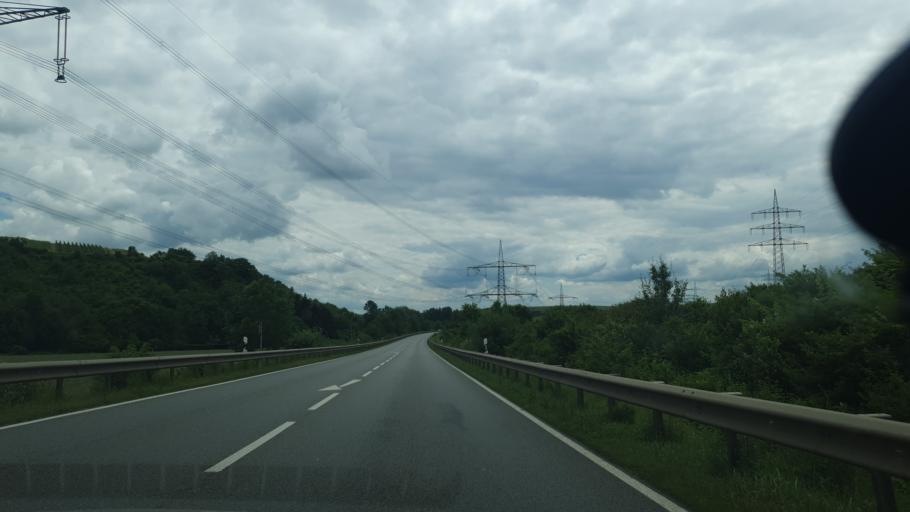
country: DE
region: Rheinland-Pfalz
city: Windesheim
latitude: 49.9104
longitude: 7.8214
